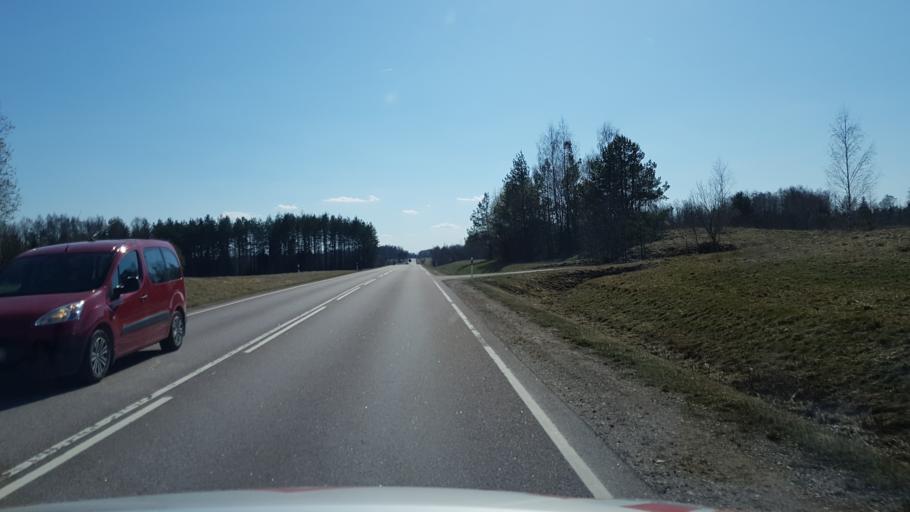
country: EE
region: Jogevamaa
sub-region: Mustvee linn
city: Mustvee
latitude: 58.7262
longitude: 26.8363
